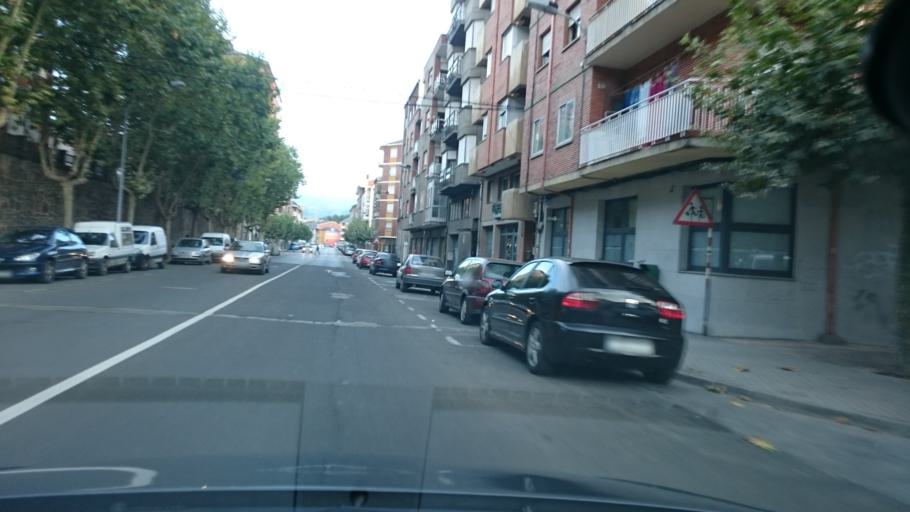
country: ES
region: Castille and Leon
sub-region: Provincia de Leon
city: Ponferrada
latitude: 42.5447
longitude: -6.6022
